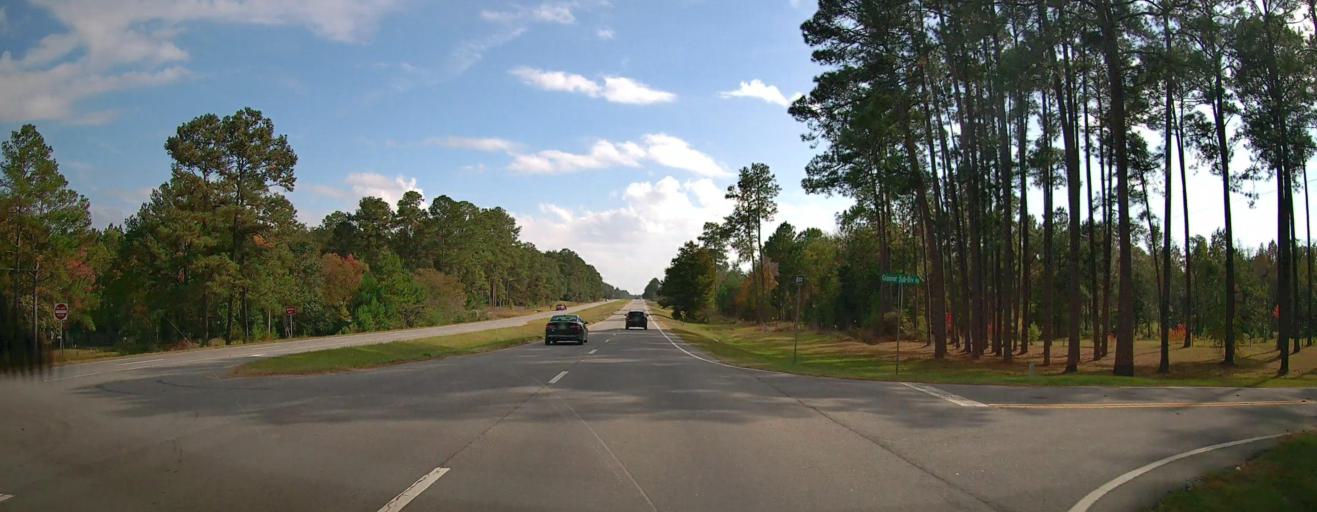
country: US
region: Georgia
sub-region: Thomas County
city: Meigs
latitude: 30.9705
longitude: -84.0341
